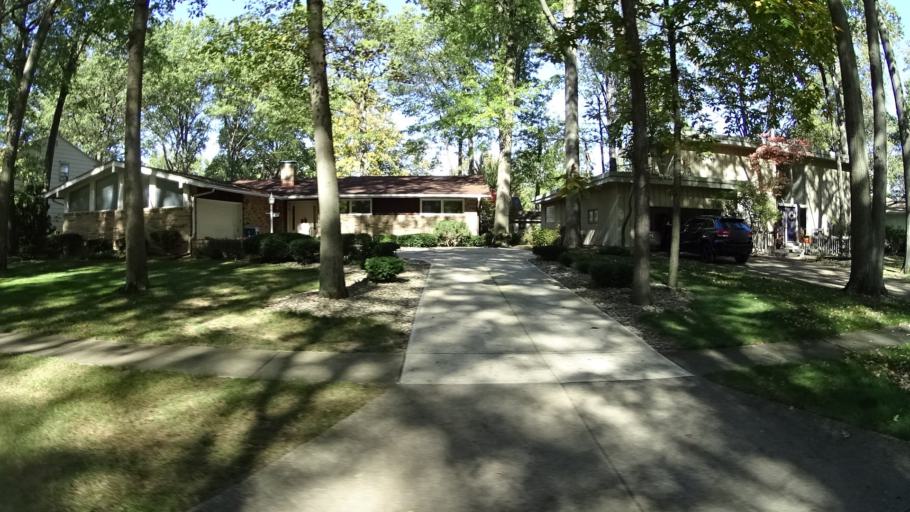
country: US
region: Ohio
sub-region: Lorain County
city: Lorain
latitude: 41.4350
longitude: -82.1772
